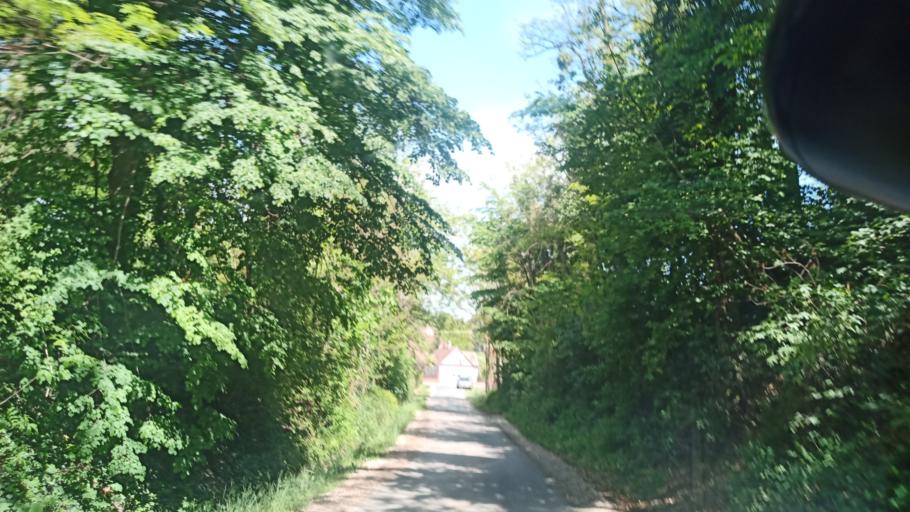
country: HU
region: Zala
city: Zalakomar
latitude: 46.6174
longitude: 17.1144
